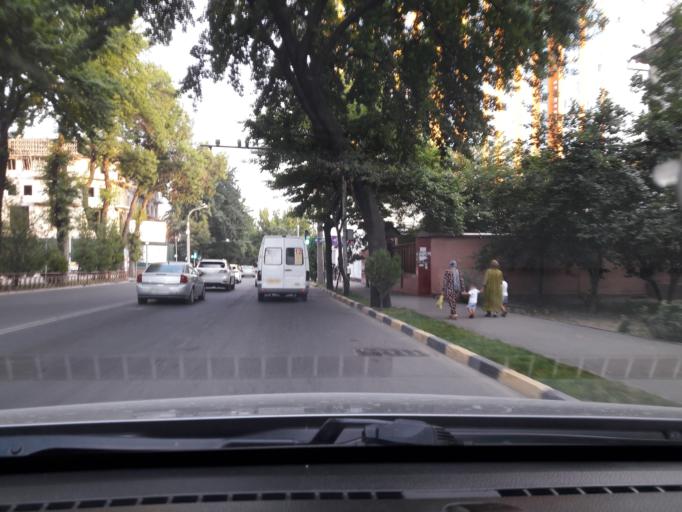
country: TJ
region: Dushanbe
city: Dushanbe
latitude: 38.5796
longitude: 68.7936
